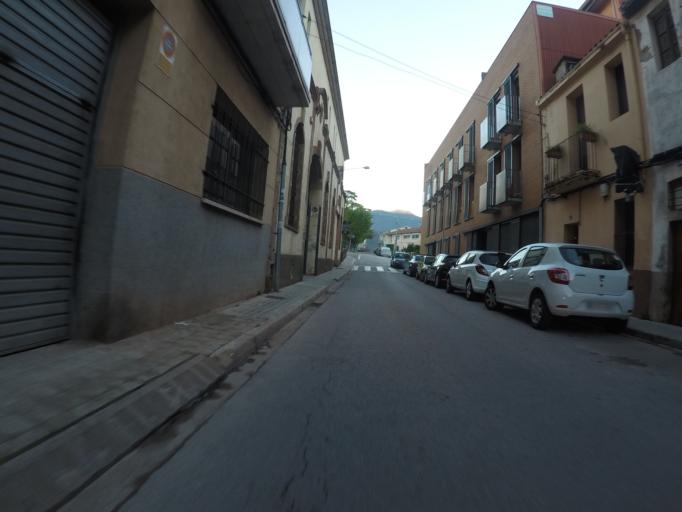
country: ES
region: Catalonia
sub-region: Provincia de Barcelona
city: Monistrol de Montserrat
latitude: 41.6098
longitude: 1.8491
